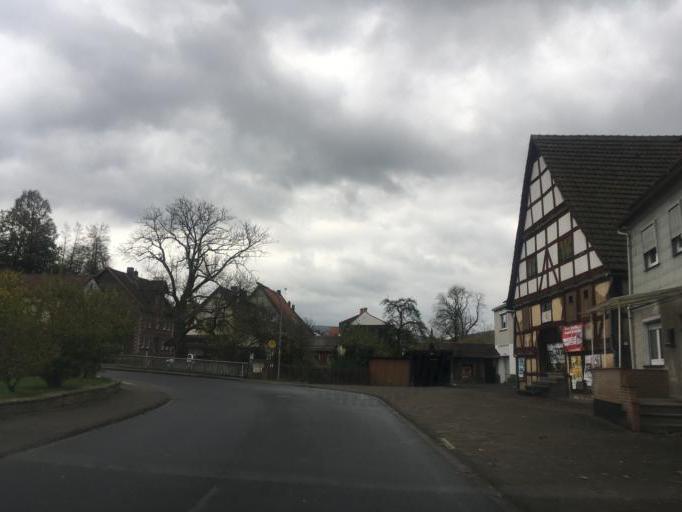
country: DE
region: Lower Saxony
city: Bodenfelde
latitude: 51.6271
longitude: 9.5566
